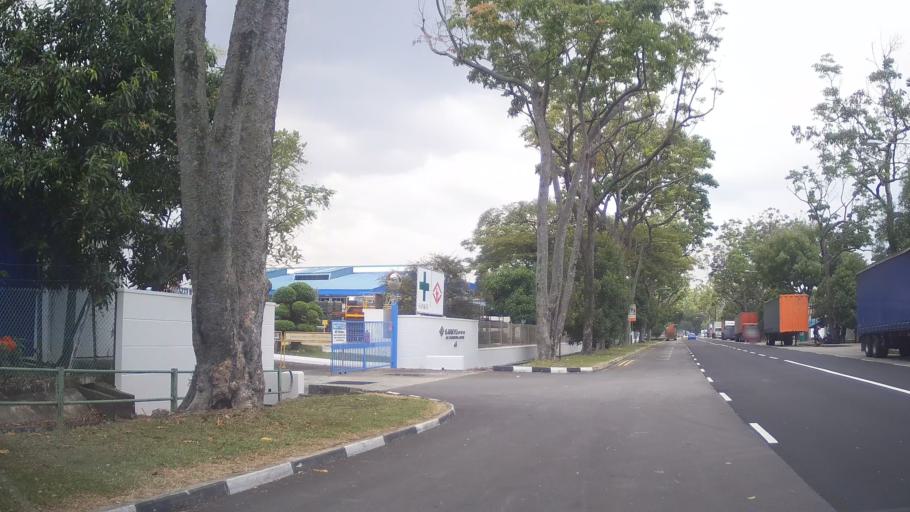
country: MY
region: Johor
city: Johor Bahru
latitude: 1.3143
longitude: 103.6666
